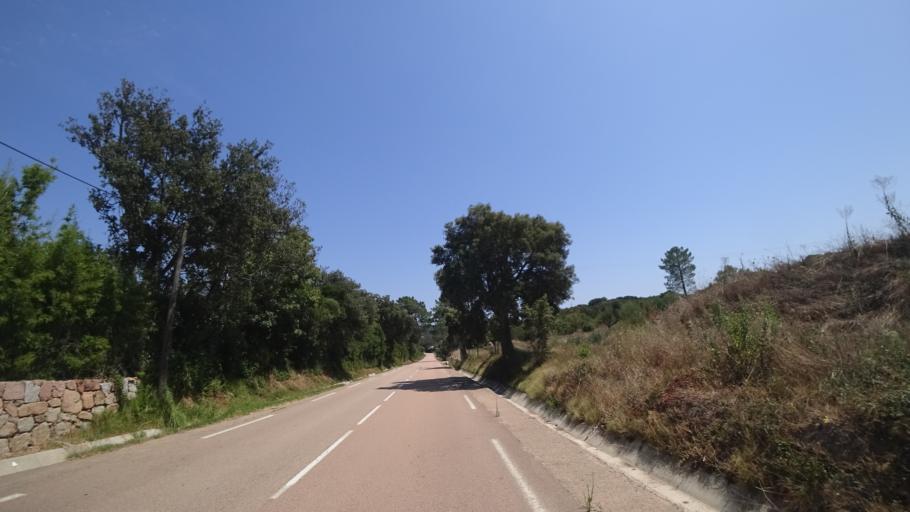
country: FR
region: Corsica
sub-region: Departement de la Corse-du-Sud
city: Porto-Vecchio
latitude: 41.6285
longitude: 9.2457
